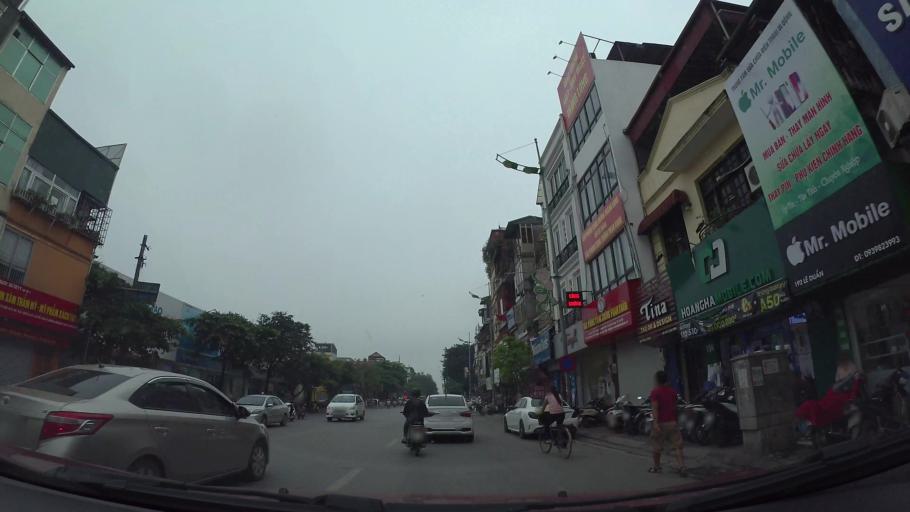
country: VN
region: Ha Noi
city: Hanoi
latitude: 21.0174
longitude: 105.8413
